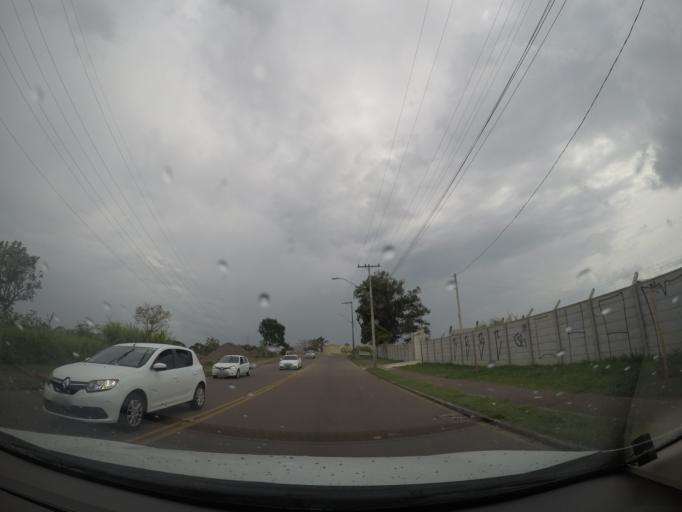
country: BR
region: Parana
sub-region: Sao Jose Dos Pinhais
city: Sao Jose dos Pinhais
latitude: -25.5069
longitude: -49.2143
